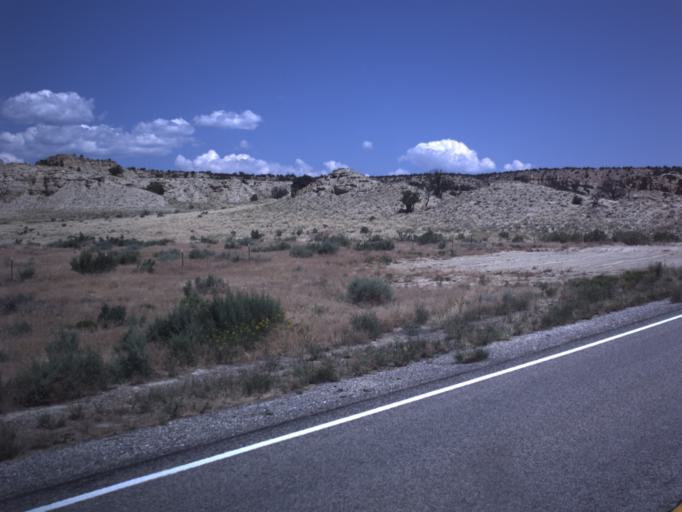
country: US
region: Utah
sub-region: Emery County
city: Ferron
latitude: 38.8199
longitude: -111.3287
